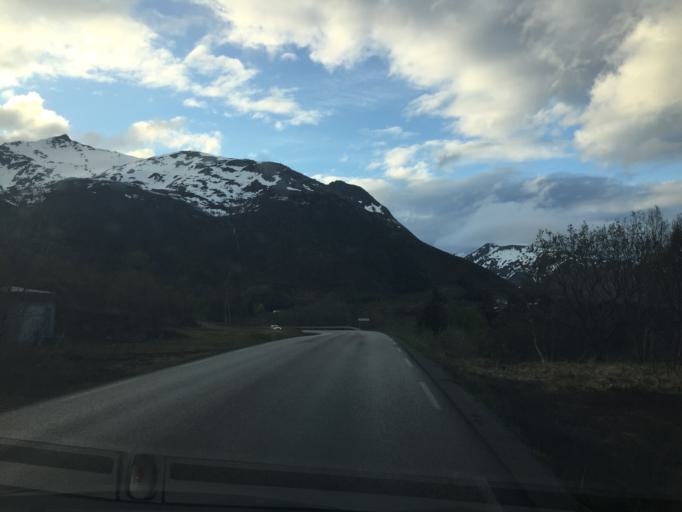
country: NO
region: Nordland
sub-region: Vagan
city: Svolvaer
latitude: 68.3223
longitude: 14.6994
